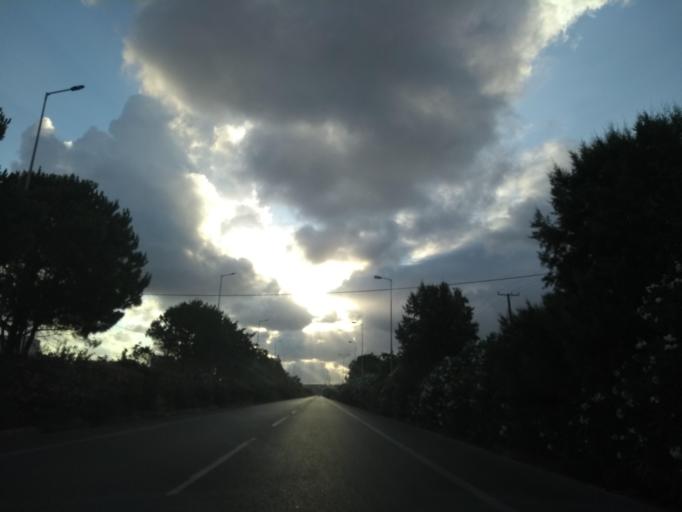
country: GR
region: Crete
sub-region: Nomos Rethymnis
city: Panormos
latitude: 35.3845
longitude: 24.5928
